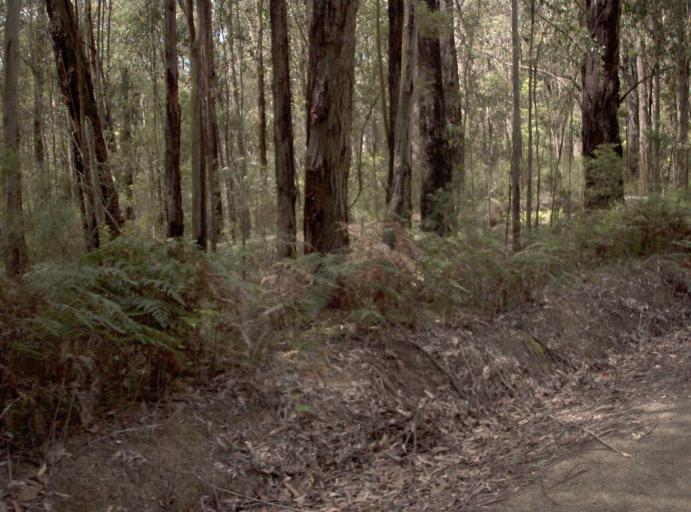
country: AU
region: New South Wales
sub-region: Bombala
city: Bombala
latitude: -37.5351
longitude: 149.3732
